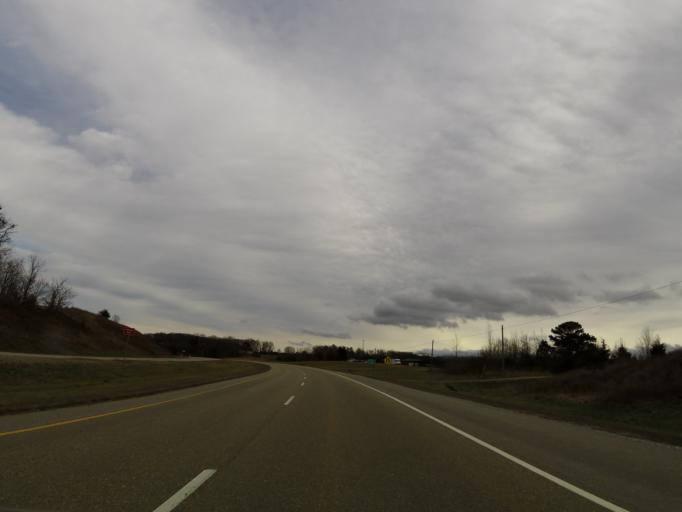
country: US
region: Tennessee
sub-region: Greene County
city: Mosheim
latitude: 36.0368
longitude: -83.0073
